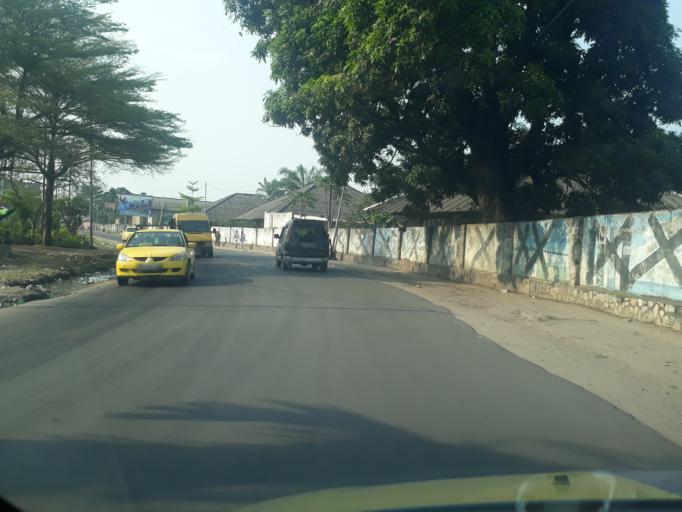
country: CD
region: Kinshasa
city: Kinshasa
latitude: -4.3151
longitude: 15.3311
